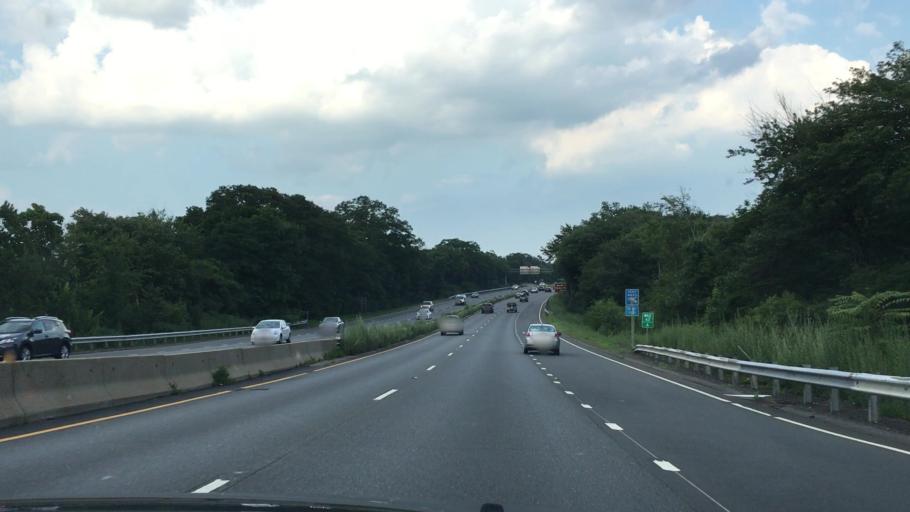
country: US
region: Massachusetts
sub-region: Essex County
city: Beverly
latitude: 42.5751
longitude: -70.8900
